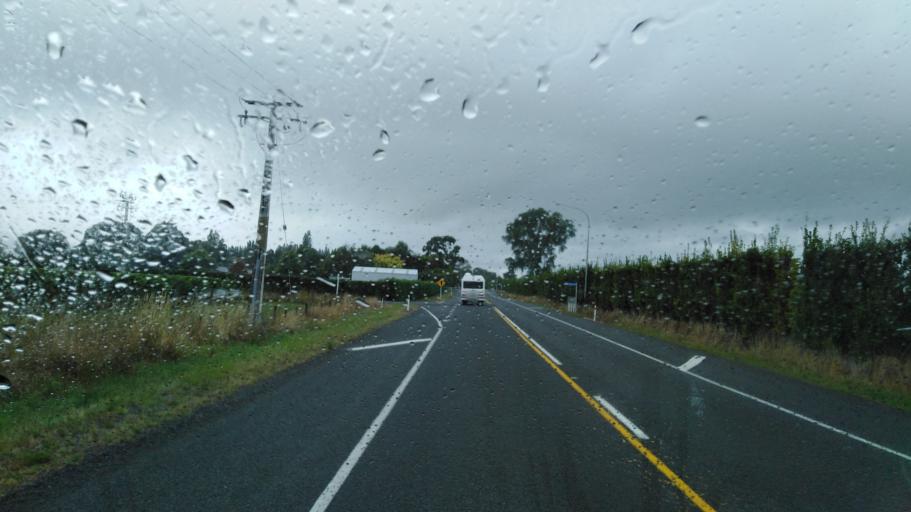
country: NZ
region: Marlborough
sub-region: Marlborough District
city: Blenheim
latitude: -41.4596
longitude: 173.9452
